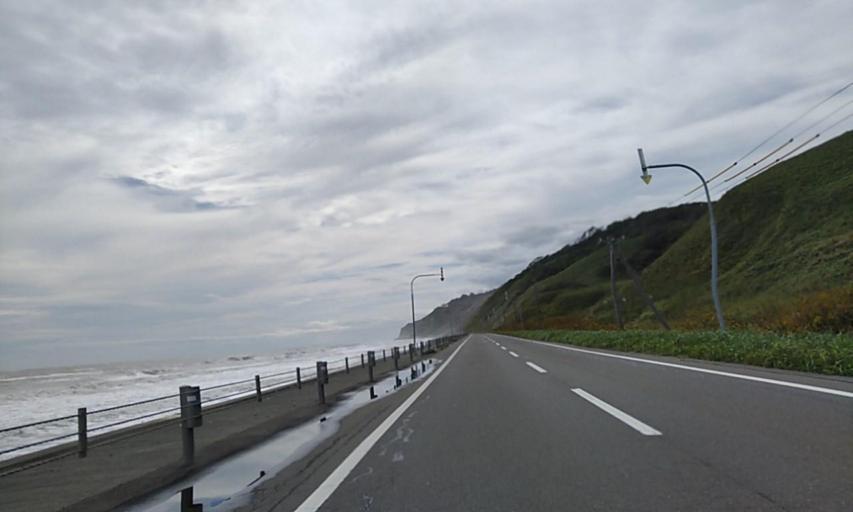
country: JP
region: Hokkaido
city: Obihiro
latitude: 42.7812
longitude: 143.7848
